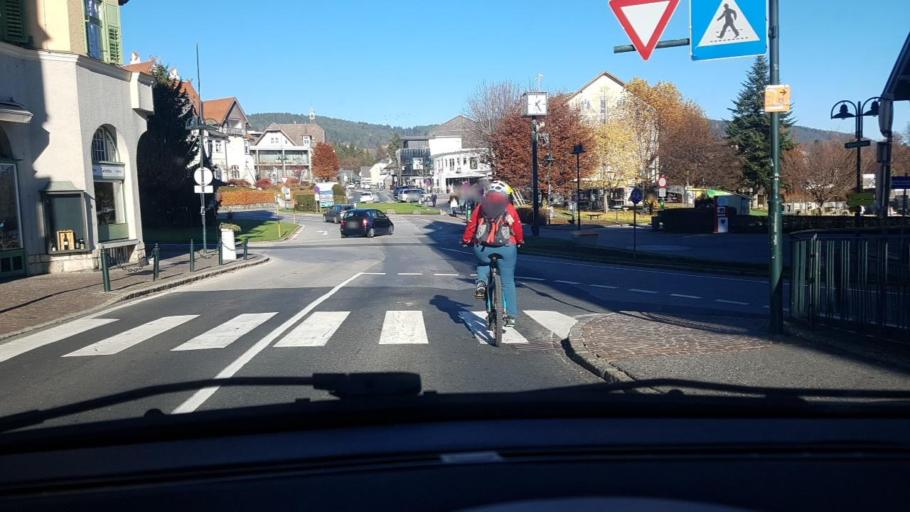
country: AT
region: Carinthia
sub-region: Politischer Bezirk Villach Land
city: Velden am Woerthersee
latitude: 46.6133
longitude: 14.0417
